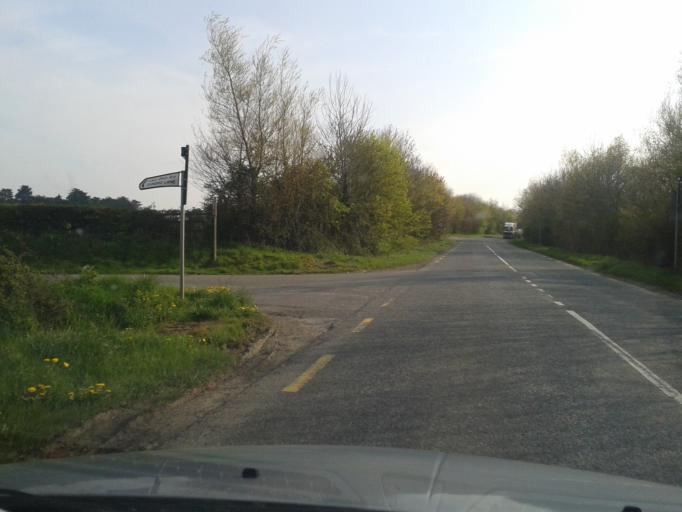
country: IE
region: Leinster
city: Ballymun
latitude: 53.4368
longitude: -6.2918
